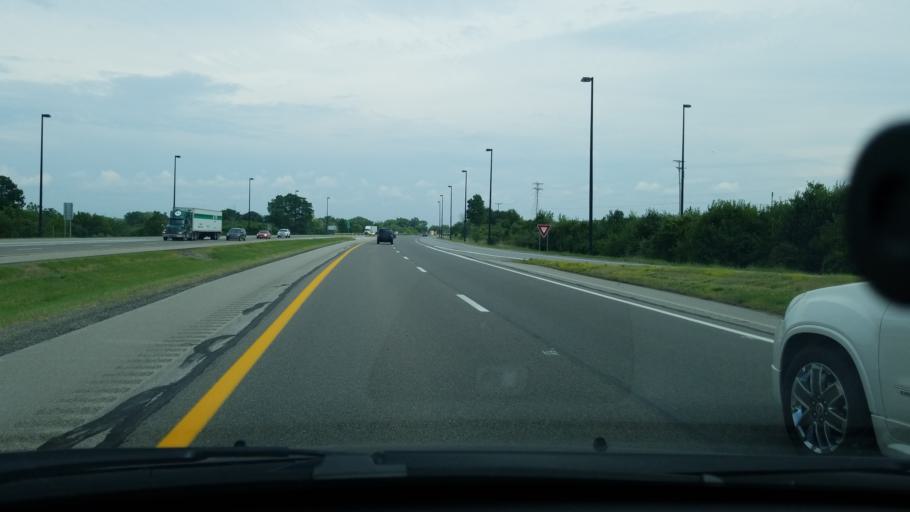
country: US
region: Ohio
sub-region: Mahoning County
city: New Middletown
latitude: 40.9390
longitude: -80.5838
